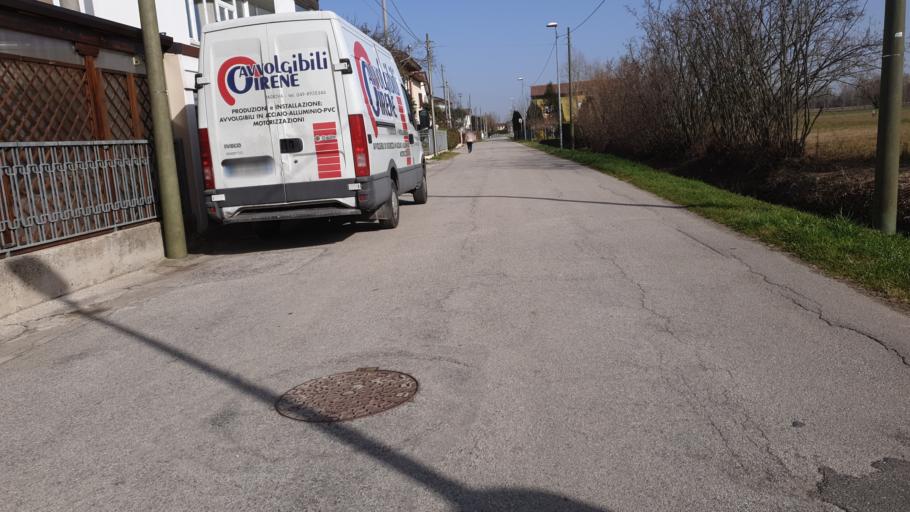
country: IT
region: Veneto
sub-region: Provincia di Padova
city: Mejaniga
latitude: 45.4677
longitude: 11.9134
